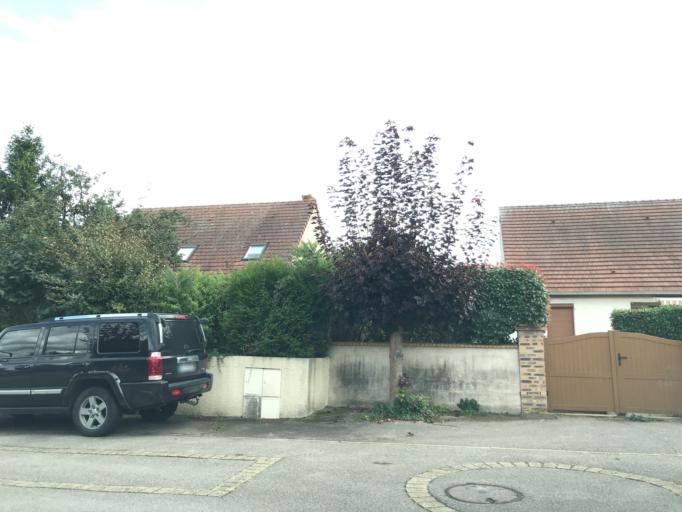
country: FR
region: Haute-Normandie
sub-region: Departement de l'Eure
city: Saint-Just
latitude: 49.1059
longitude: 1.4439
